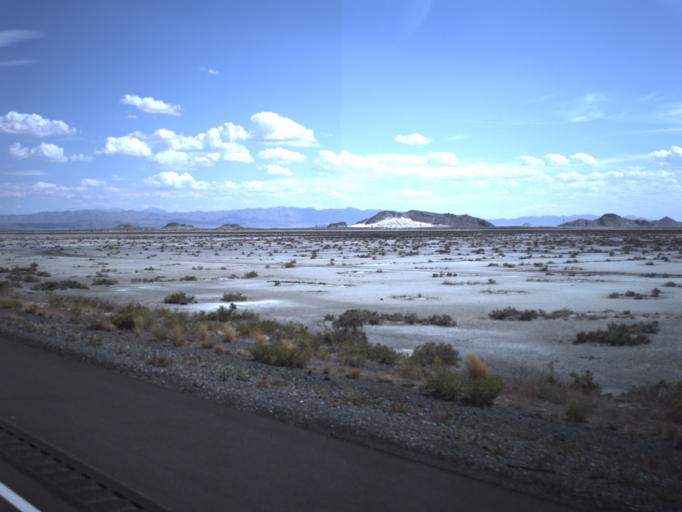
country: US
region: Utah
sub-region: Tooele County
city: Wendover
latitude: 40.7274
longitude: -113.3188
